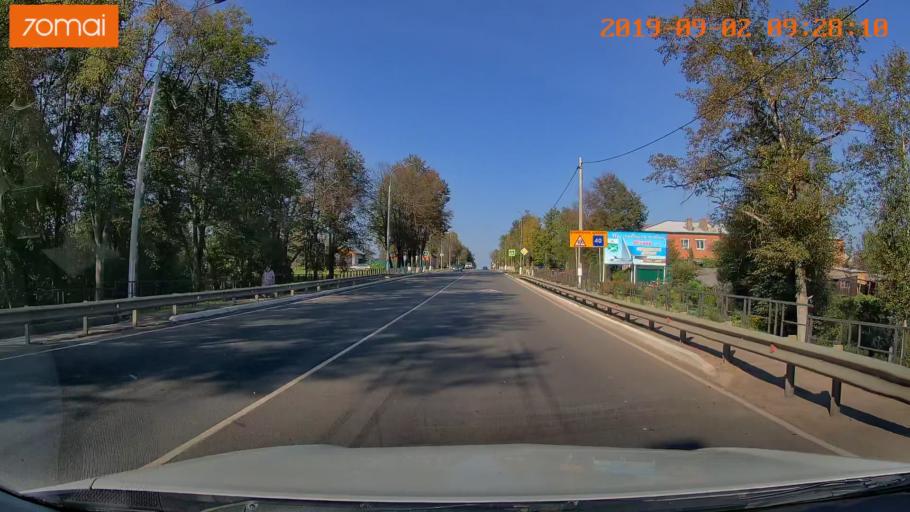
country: RU
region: Kaluga
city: Yukhnov
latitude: 54.7440
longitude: 35.2336
